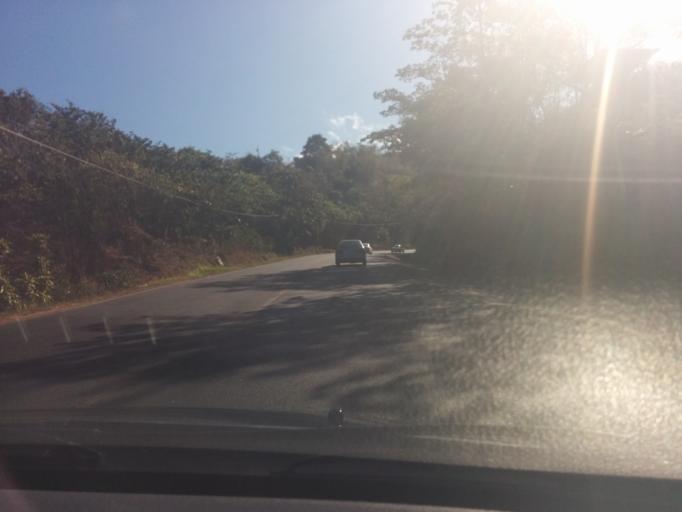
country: CR
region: Alajuela
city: San Rafael
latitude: 10.0369
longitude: -84.5088
